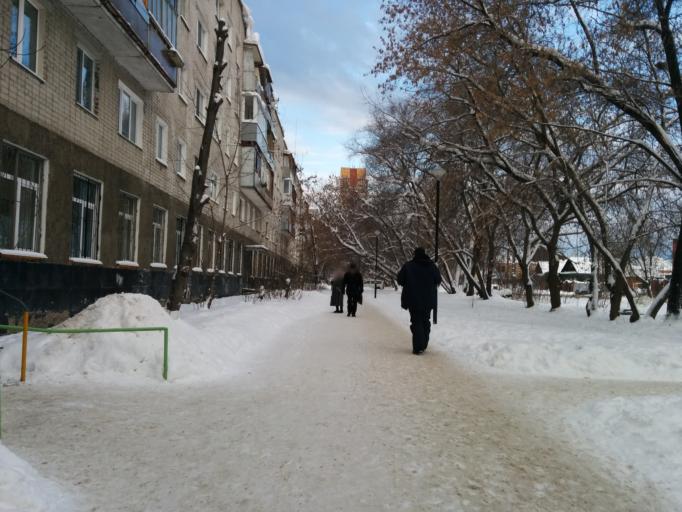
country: RU
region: Perm
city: Perm
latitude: 57.9836
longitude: 56.2917
